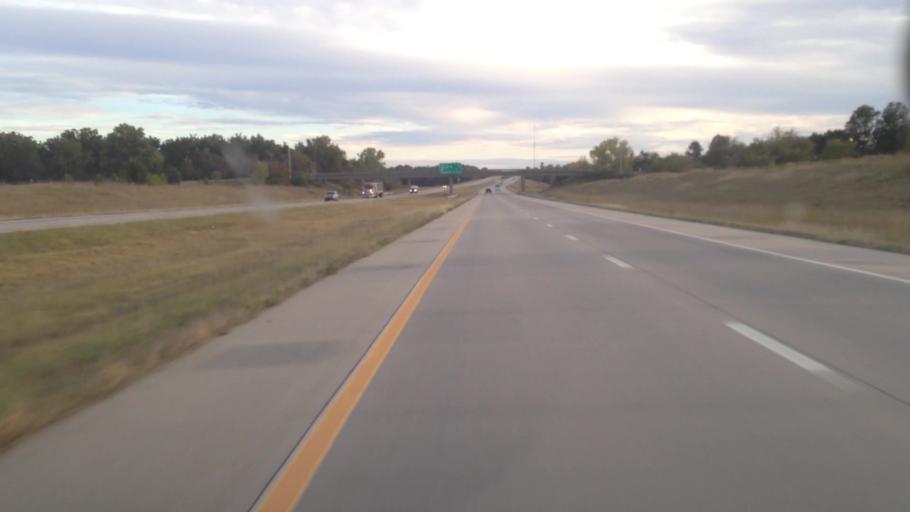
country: US
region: Kansas
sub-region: Franklin County
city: Ottawa
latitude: 38.6110
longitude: -95.2327
